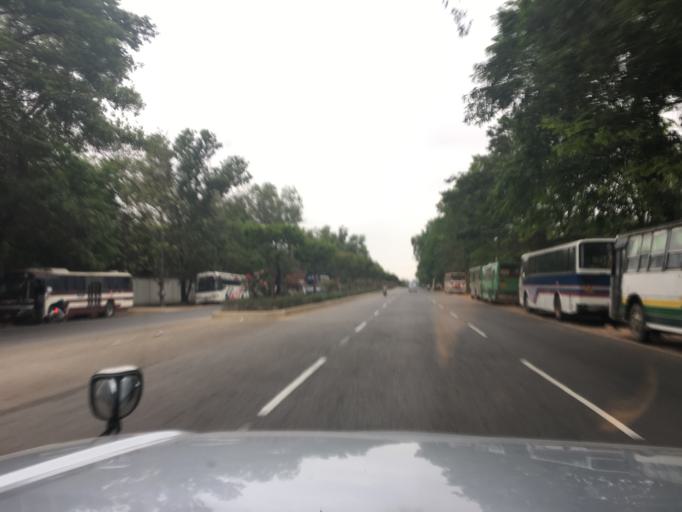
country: MM
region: Bago
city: Bago
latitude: 17.2398
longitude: 96.4634
